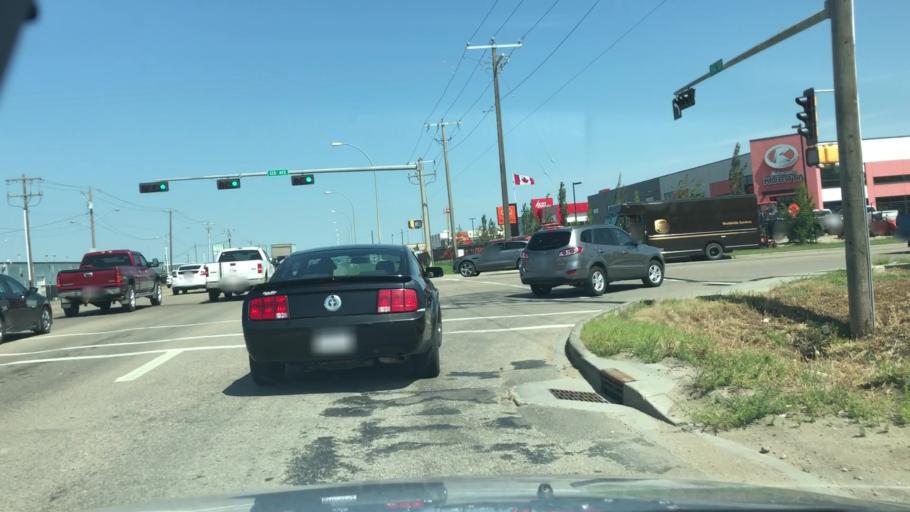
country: CA
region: Alberta
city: St. Albert
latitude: 53.5845
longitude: -113.5902
